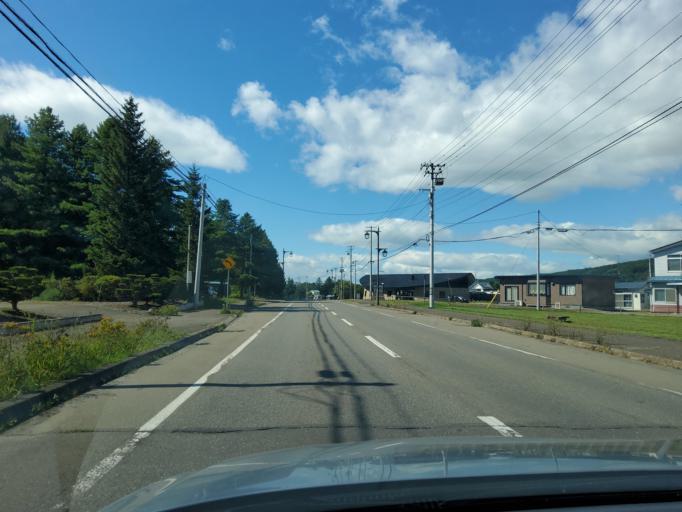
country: JP
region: Hokkaido
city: Obihiro
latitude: 42.9334
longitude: 143.2992
